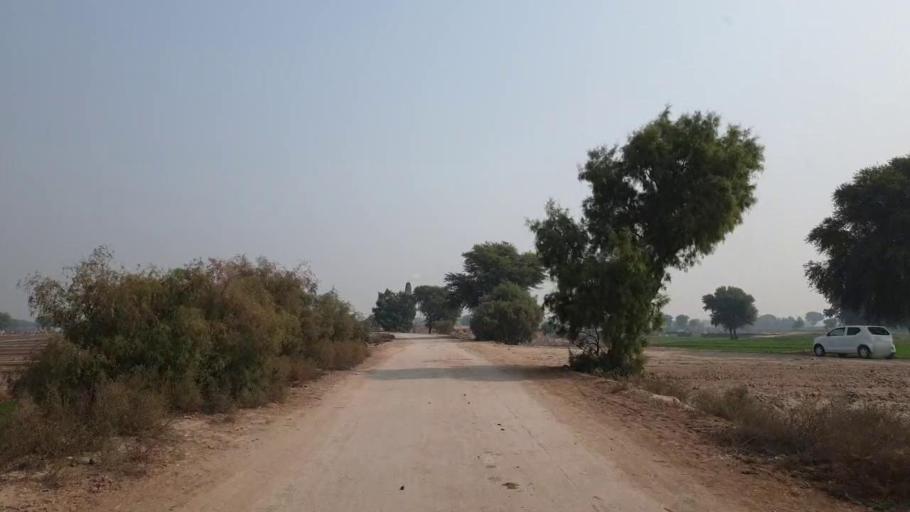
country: PK
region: Sindh
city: Bhan
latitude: 26.5166
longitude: 67.7241
